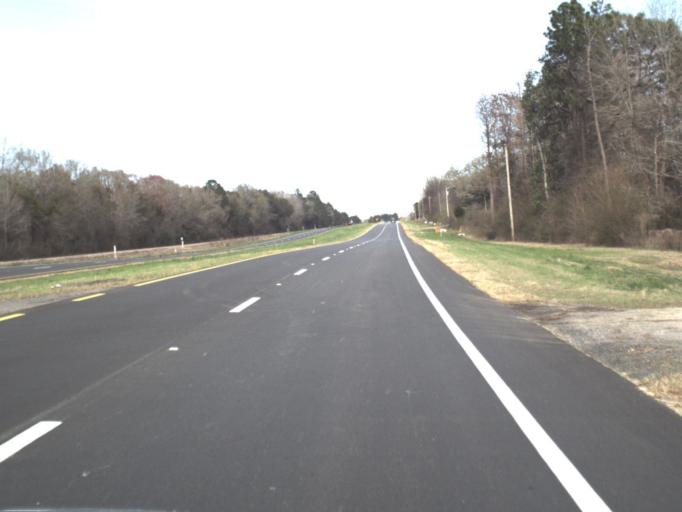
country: US
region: Florida
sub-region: Washington County
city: Chipley
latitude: 30.6751
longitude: -85.3940
